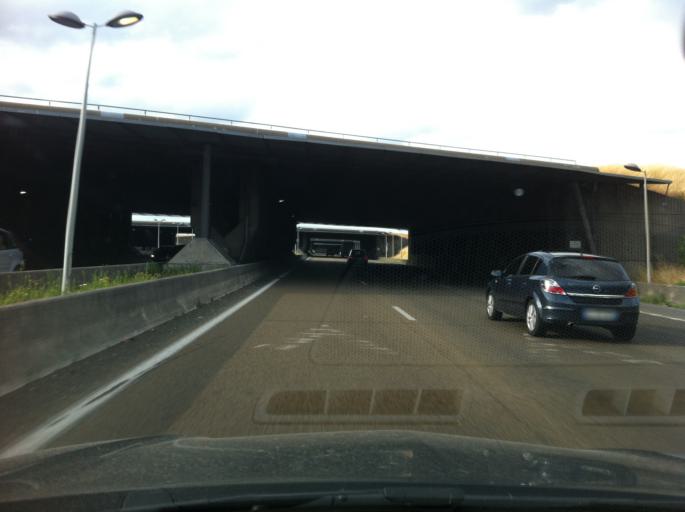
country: FR
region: Ile-de-France
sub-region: Departement du Val-d'Oise
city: Roissy-en-France
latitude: 49.0161
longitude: 2.5317
